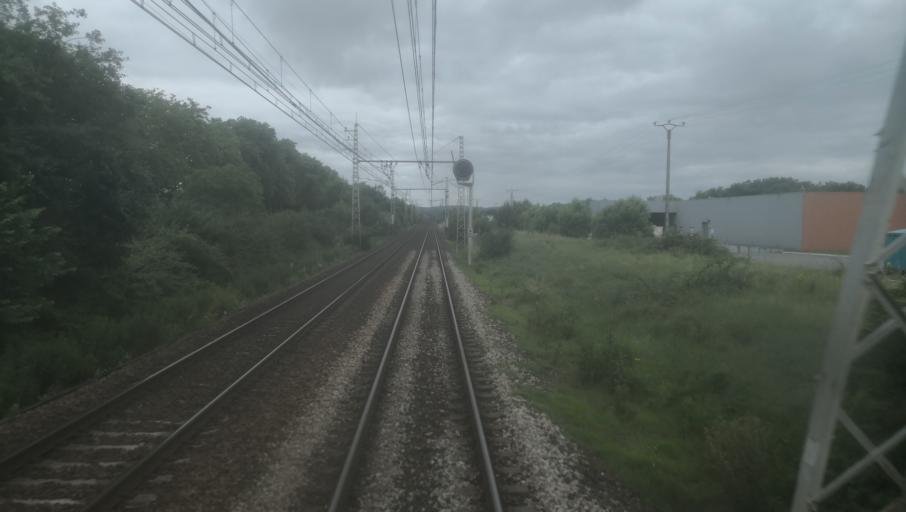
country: FR
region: Midi-Pyrenees
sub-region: Departement de la Haute-Garonne
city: Saint-Jory
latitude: 43.7456
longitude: 1.3653
